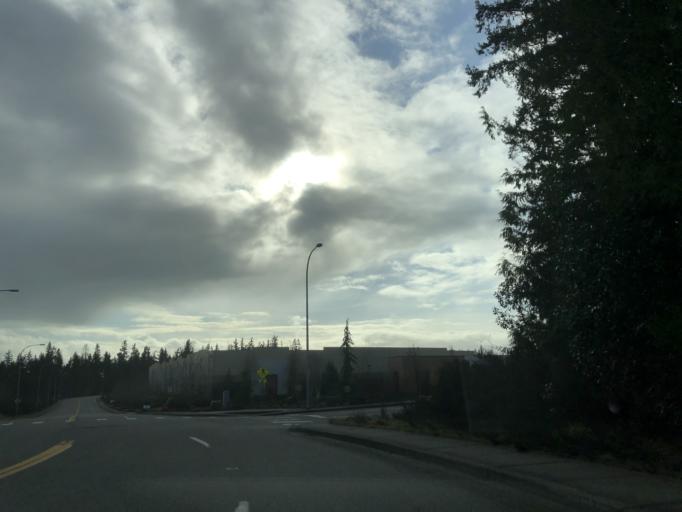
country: US
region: Washington
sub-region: Kitsap County
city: Poulsbo
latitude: 47.7655
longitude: -122.6555
